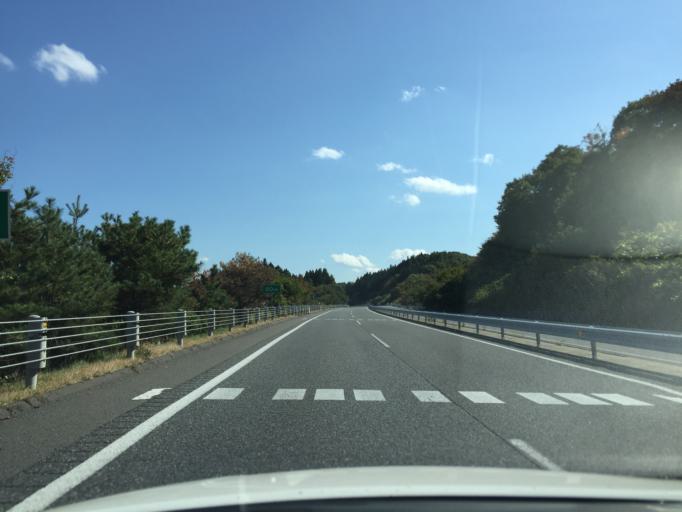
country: JP
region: Fukushima
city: Funehikimachi-funehiki
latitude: 37.2513
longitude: 140.6589
